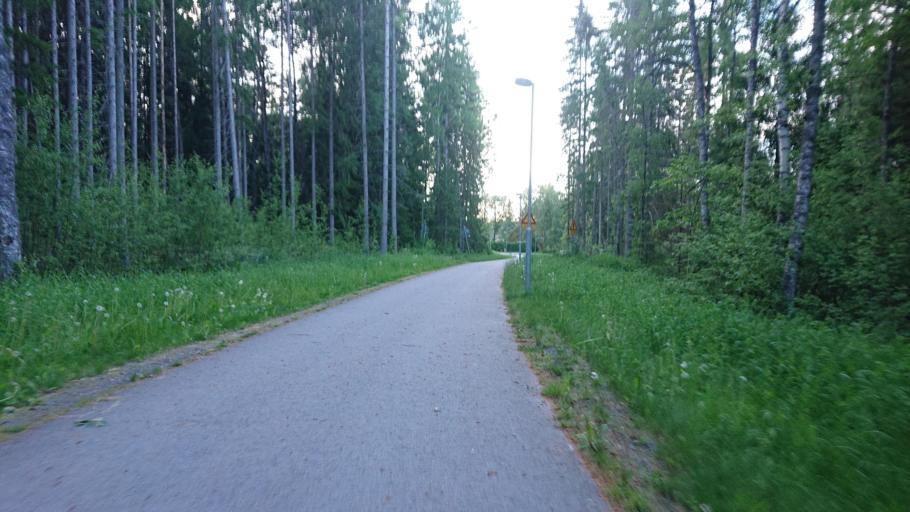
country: SE
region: Stockholm
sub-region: Osterakers Kommun
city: Akersberga
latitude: 59.4921
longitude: 18.3127
